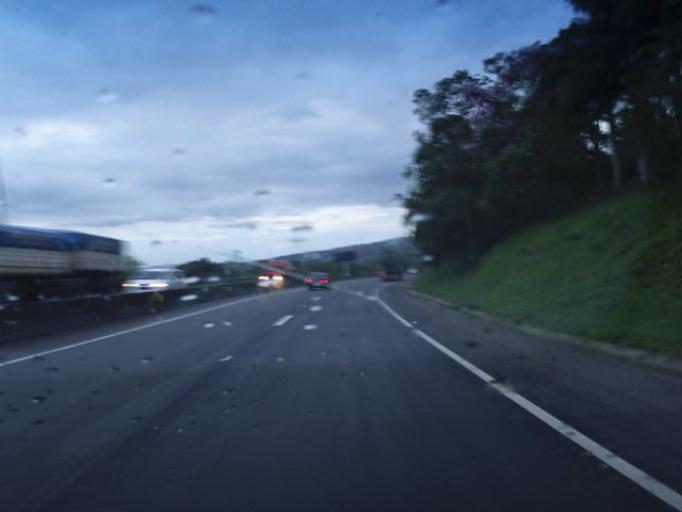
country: BR
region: Santa Catarina
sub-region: Joinville
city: Joinville
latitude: -25.9828
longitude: -48.8856
